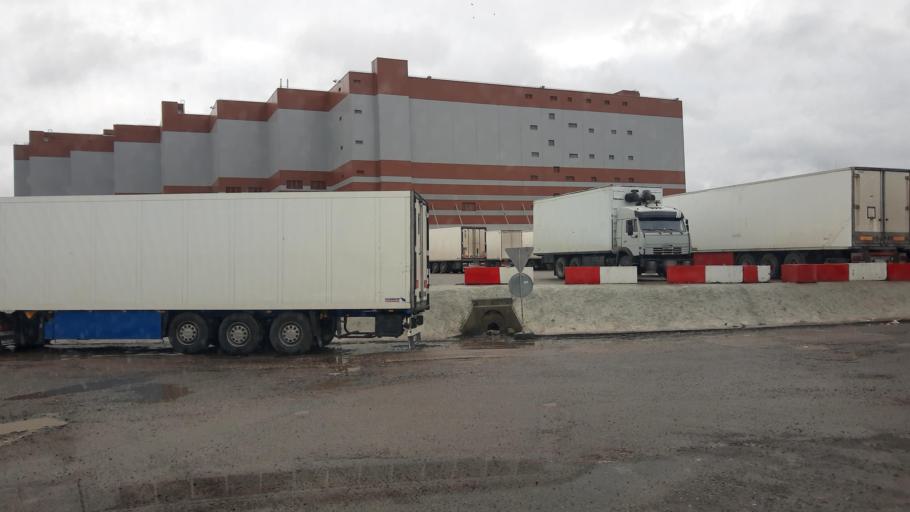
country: RU
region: Moskovskaya
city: Mosrentgen
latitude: 55.6001
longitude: 37.4570
